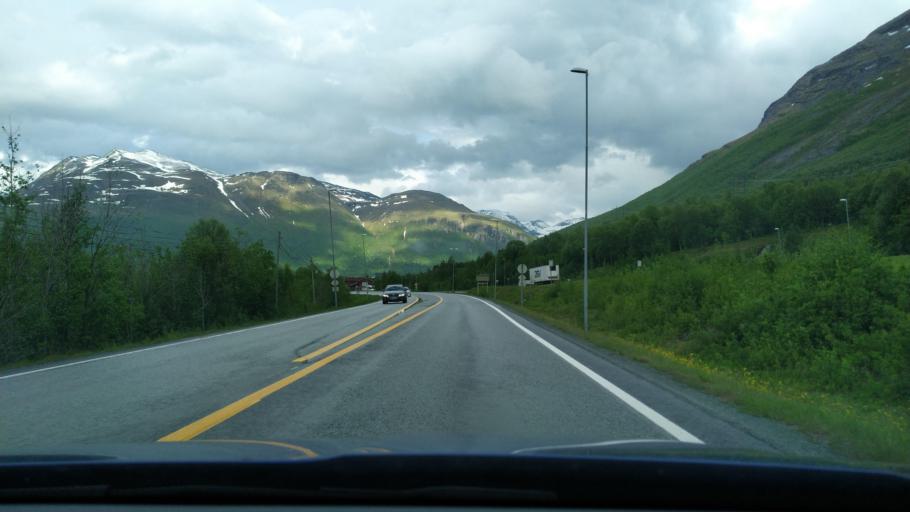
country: NO
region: Troms
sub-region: Balsfjord
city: Storsteinnes
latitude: 69.2132
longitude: 19.5313
